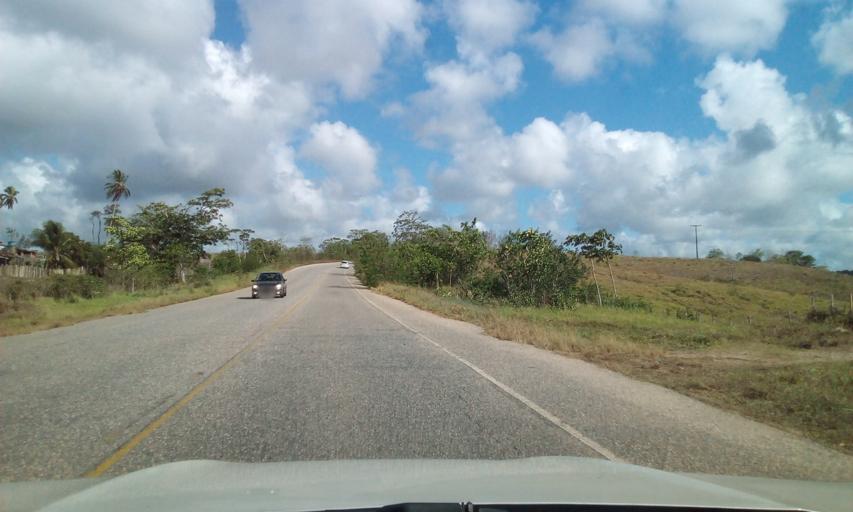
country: BR
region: Sergipe
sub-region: Estancia
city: Estancia
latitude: -11.3465
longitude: -37.4493
